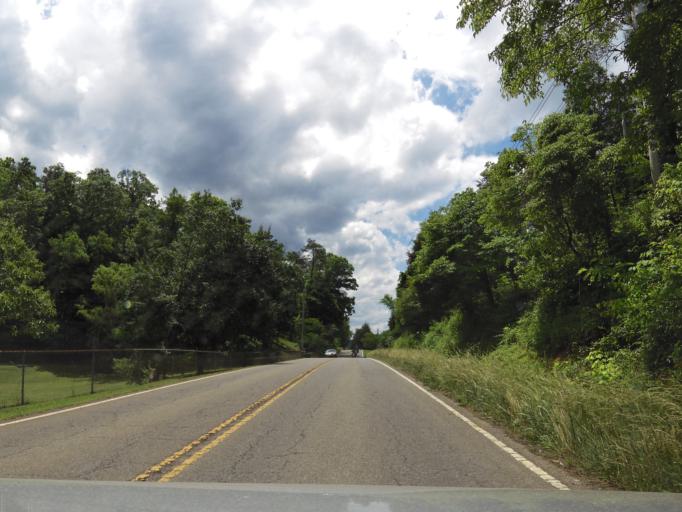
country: US
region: Tennessee
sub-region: Loudon County
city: Greenback
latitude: 35.5950
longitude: -84.0960
